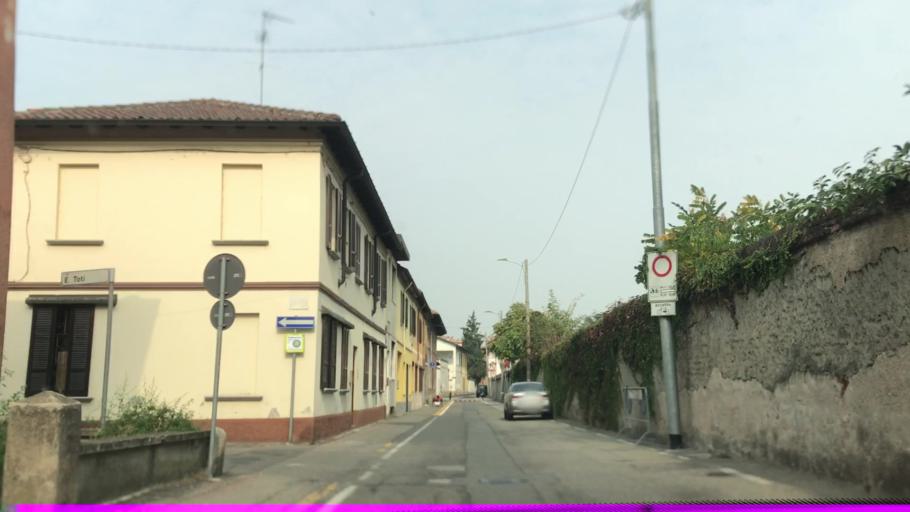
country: IT
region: Lombardy
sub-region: Citta metropolitana di Milano
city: Corbetta
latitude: 45.4638
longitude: 8.9183
